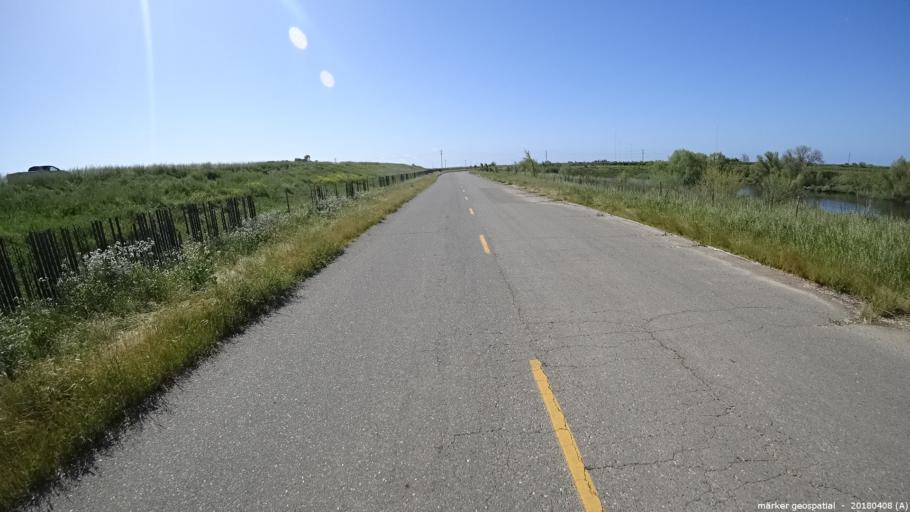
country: US
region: California
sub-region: Sacramento County
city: Walnut Grove
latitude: 38.3237
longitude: -121.4667
